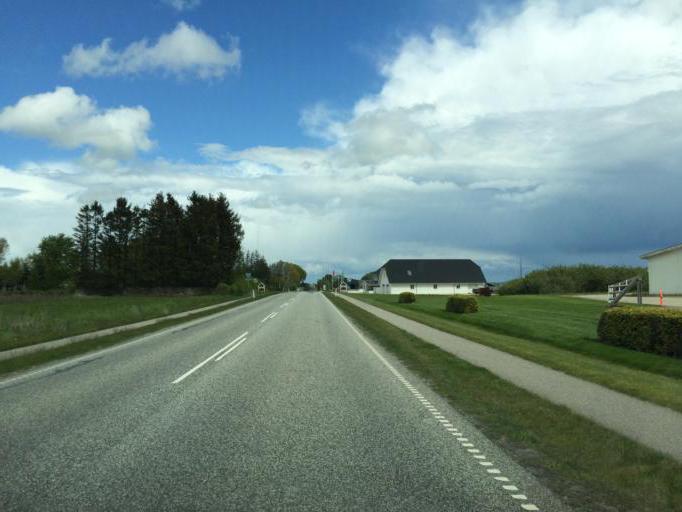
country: DK
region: North Denmark
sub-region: Vesthimmerland Kommune
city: Farso
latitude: 56.7608
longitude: 9.3344
